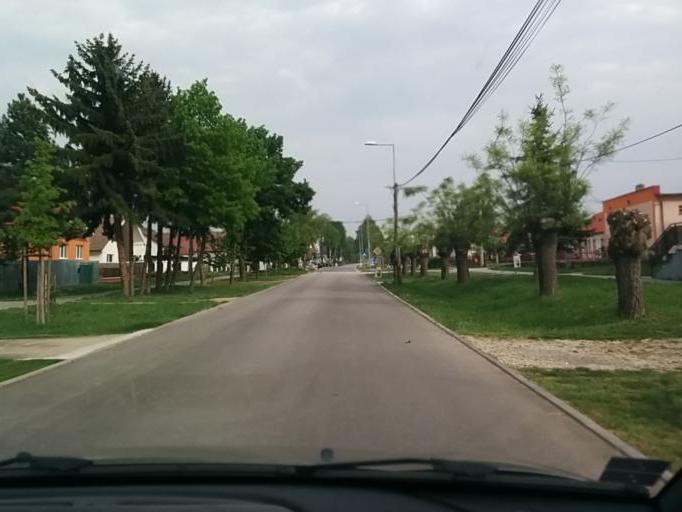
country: SK
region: Trnavsky
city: Sladkovicovo
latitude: 48.2515
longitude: 17.6155
